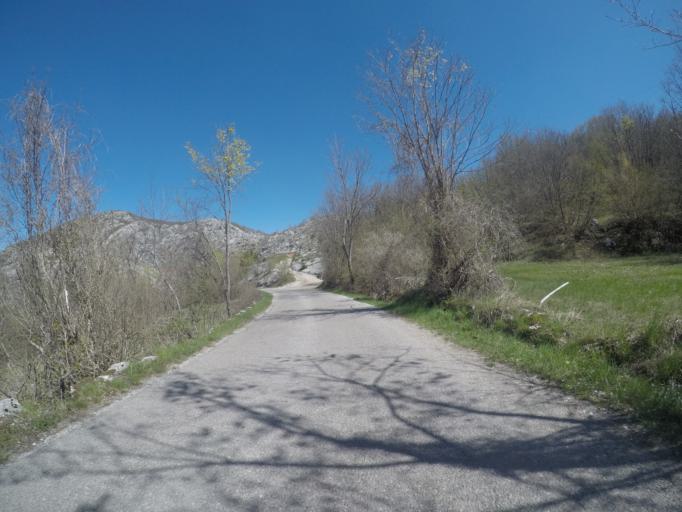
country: ME
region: Cetinje
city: Cetinje
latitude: 42.4560
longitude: 18.8737
